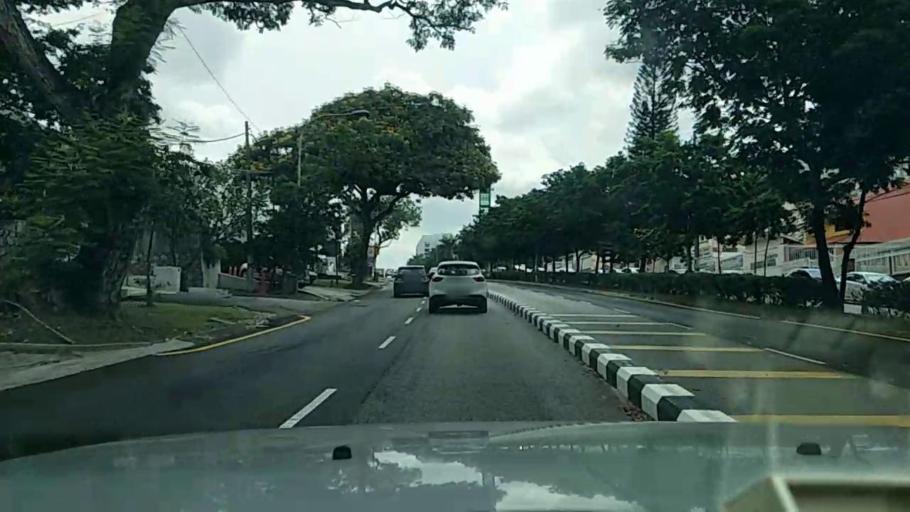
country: MY
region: Kuala Lumpur
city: Kuala Lumpur
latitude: 3.1425
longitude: 101.6696
